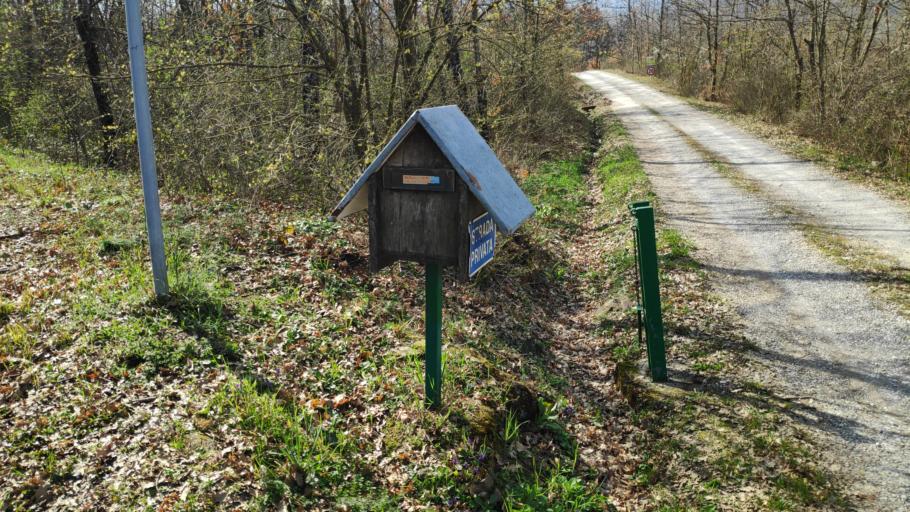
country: IT
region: Emilia-Romagna
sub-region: Provincia di Bologna
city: Berzantina
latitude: 44.1745
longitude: 10.9956
